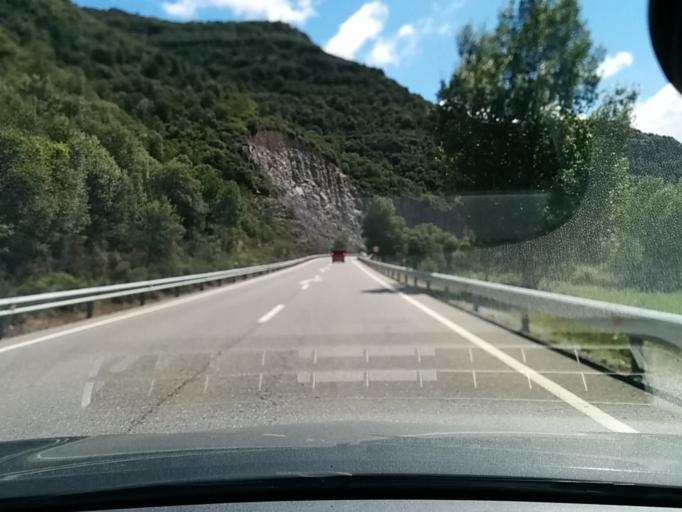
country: ES
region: Aragon
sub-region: Provincia de Huesca
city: Boltana
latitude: 42.4660
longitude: 0.0291
